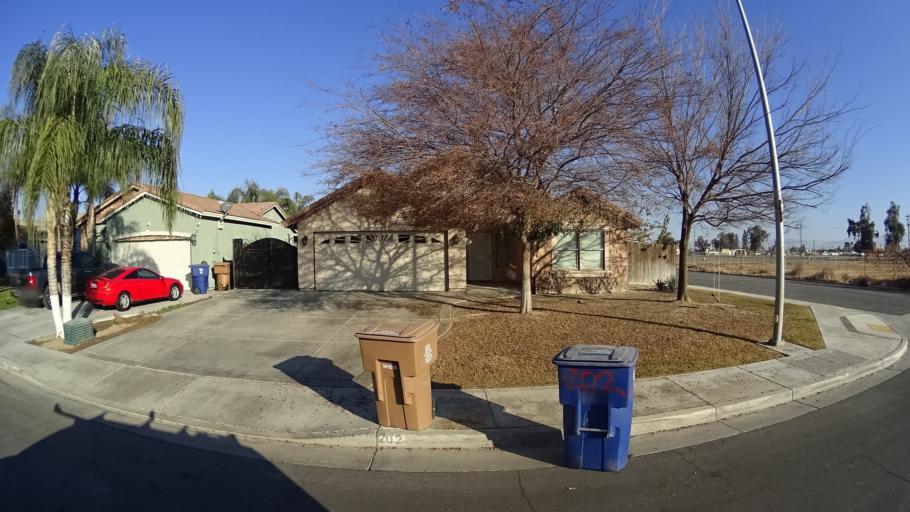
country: US
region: California
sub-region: Kern County
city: Greenfield
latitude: 35.2990
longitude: -119.0048
